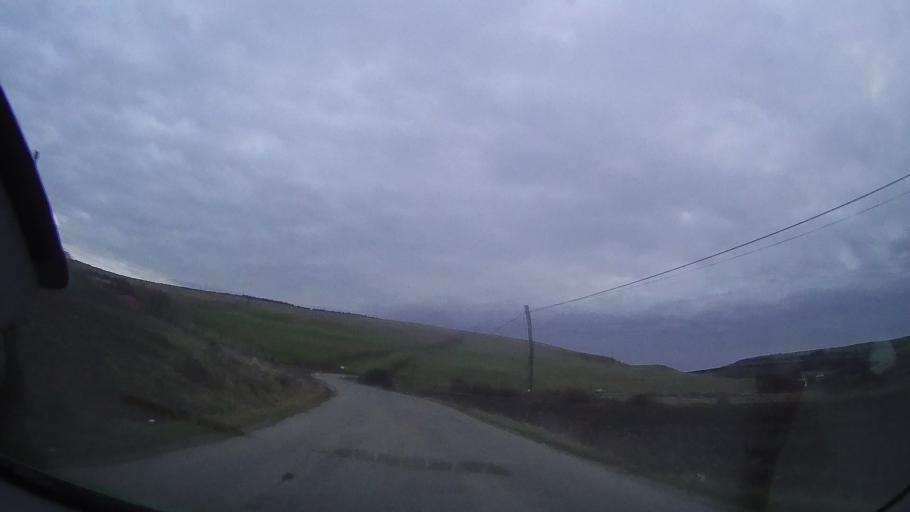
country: RO
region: Cluj
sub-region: Comuna Caianu
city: Vaida-Camaras
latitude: 46.8170
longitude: 23.9352
